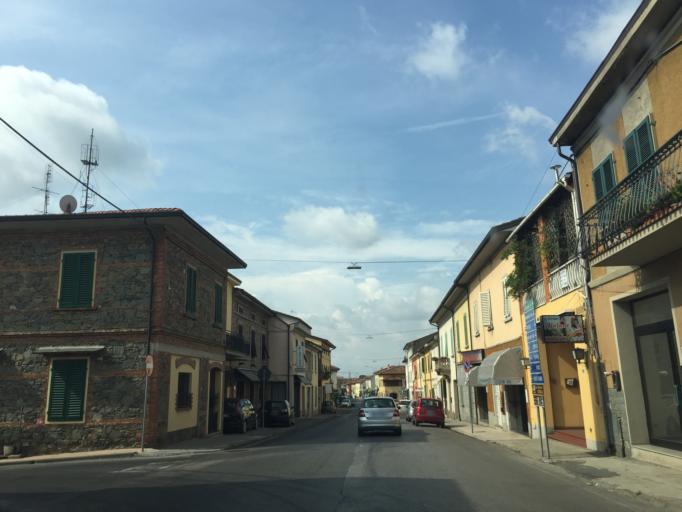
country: IT
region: Tuscany
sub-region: Provincia di Pistoia
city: Lamporecchio
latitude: 43.8120
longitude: 10.8916
